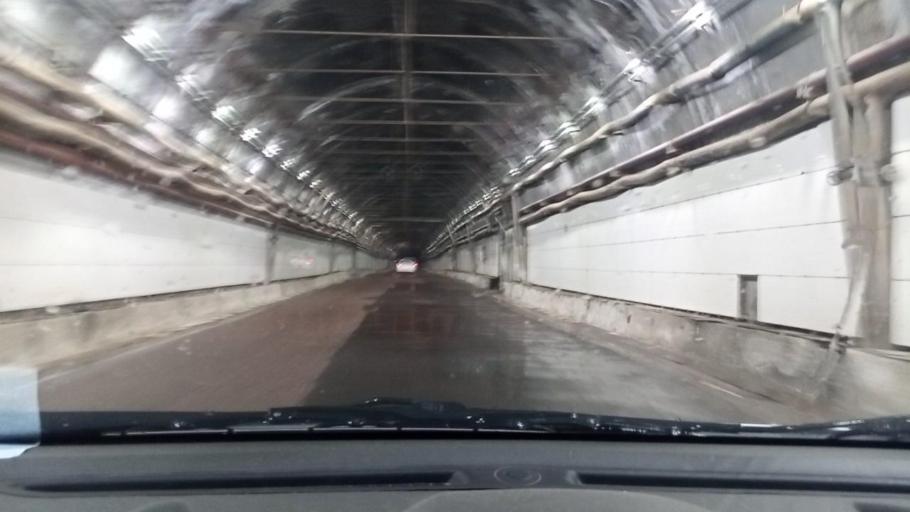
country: UZ
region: Toshkent
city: Angren
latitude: 41.1023
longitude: 70.5144
